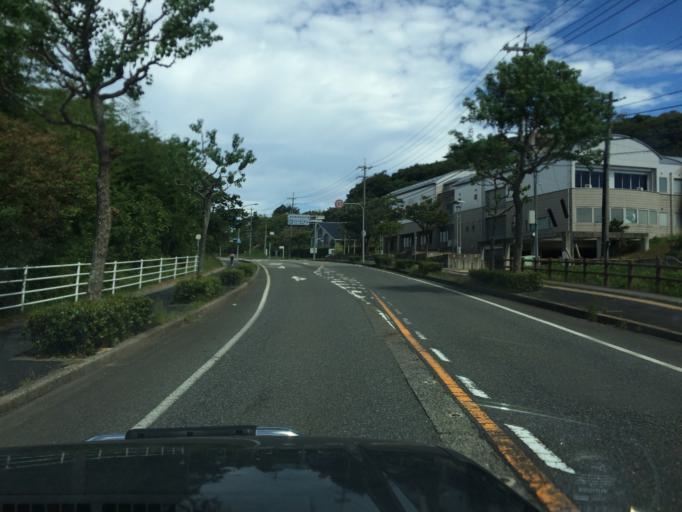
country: JP
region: Tottori
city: Kurayoshi
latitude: 35.5197
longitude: 134.0003
